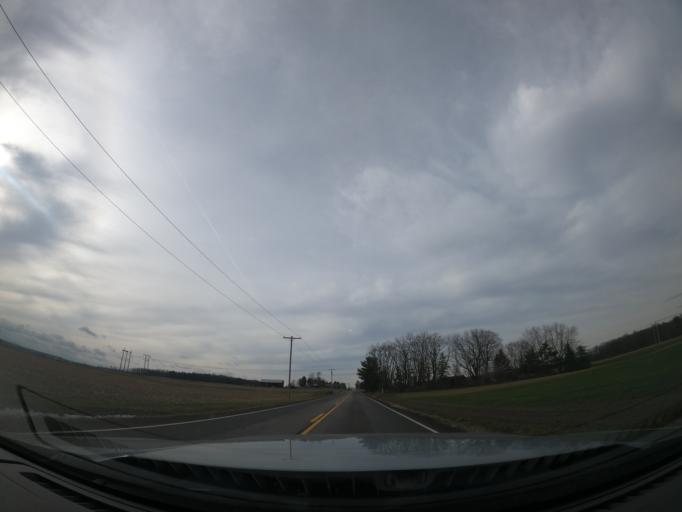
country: US
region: New York
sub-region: Yates County
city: Dundee
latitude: 42.5001
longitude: -76.9363
